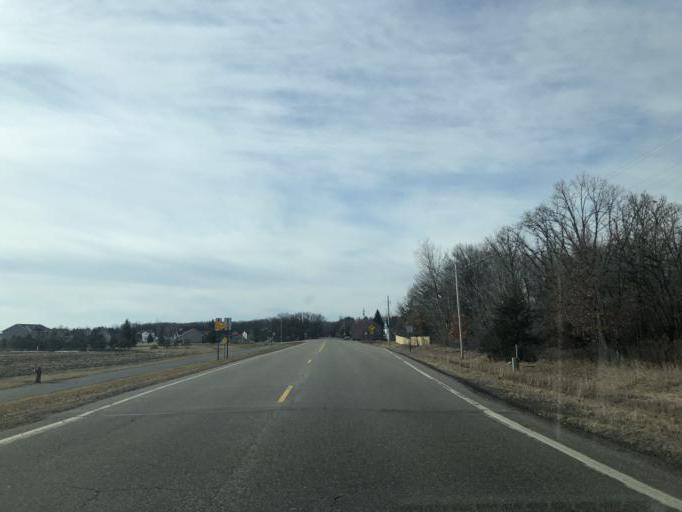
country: US
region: Minnesota
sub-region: Sherburne County
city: Becker
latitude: 45.3987
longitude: -93.8498
